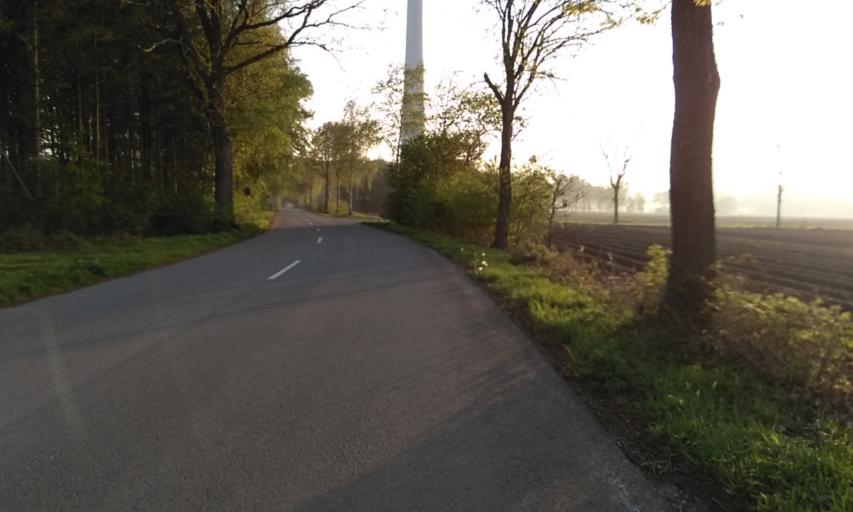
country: DE
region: Lower Saxony
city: Deinste
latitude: 53.5077
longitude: 9.4648
